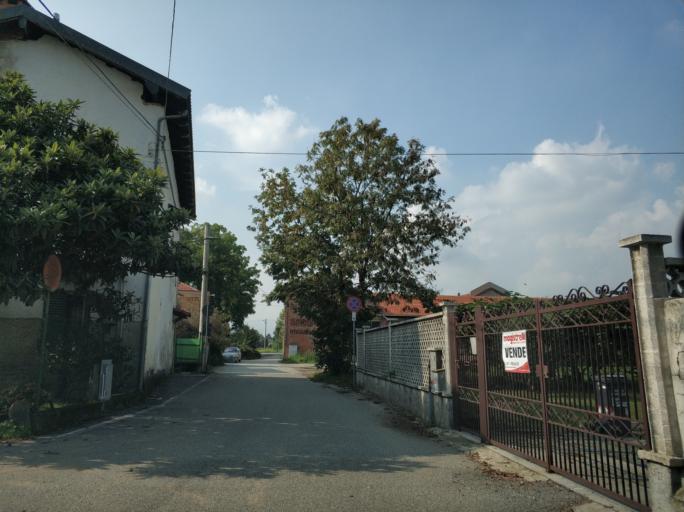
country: IT
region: Piedmont
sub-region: Provincia di Torino
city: Cirie
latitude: 45.2160
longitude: 7.5947
